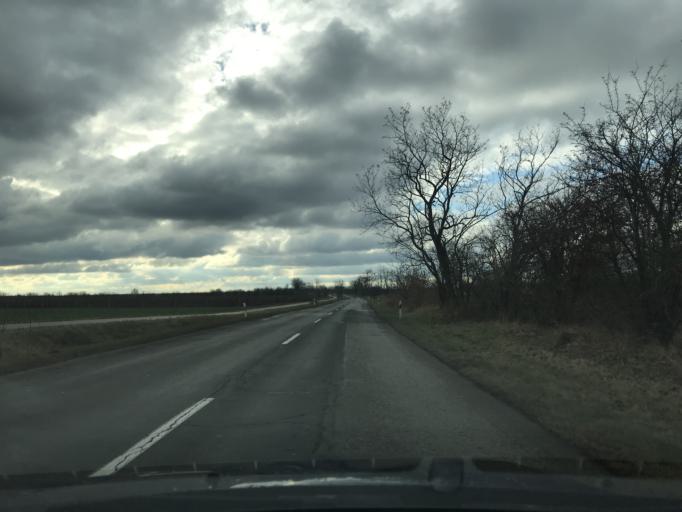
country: HU
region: Bacs-Kiskun
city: Hajos
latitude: 46.3792
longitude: 19.1400
